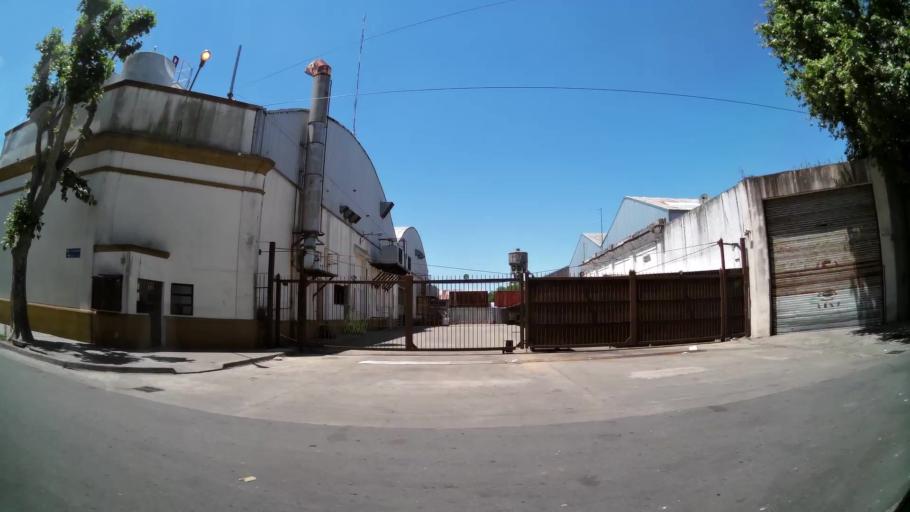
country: AR
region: Buenos Aires
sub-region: Partido de Avellaneda
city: Avellaneda
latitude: -34.6597
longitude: -58.3916
